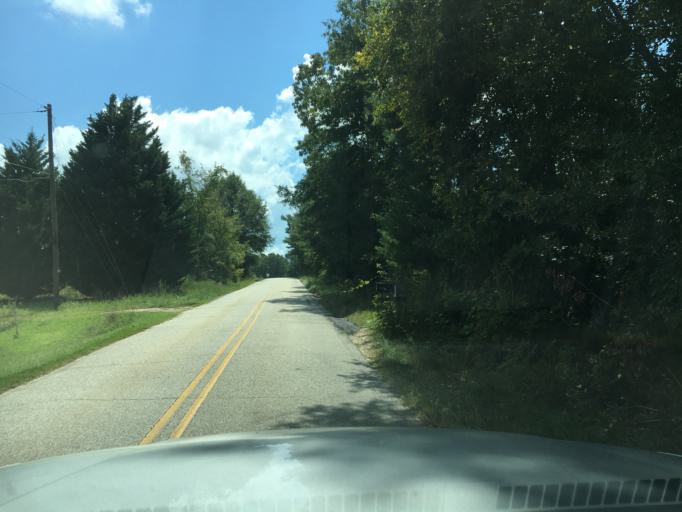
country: US
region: South Carolina
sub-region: Spartanburg County
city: Wellford
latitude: 34.8840
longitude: -82.0594
